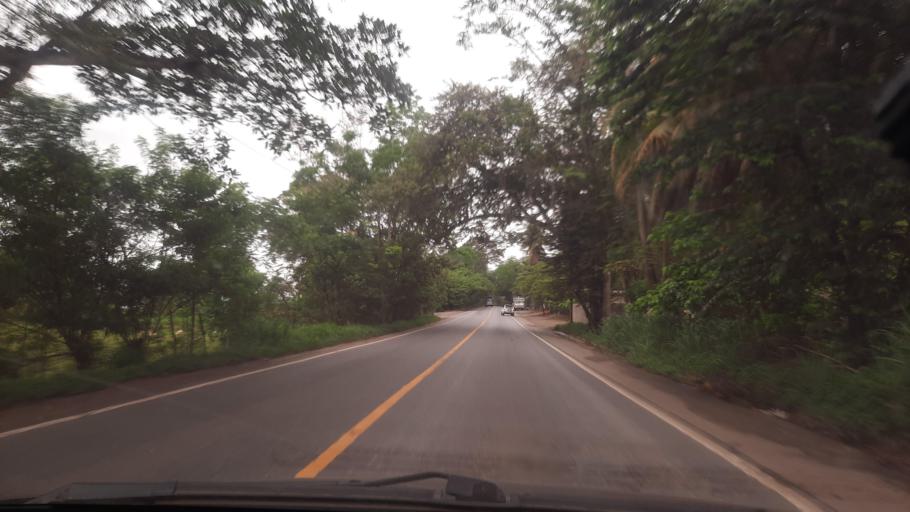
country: GT
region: Izabal
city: Morales
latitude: 15.4322
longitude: -88.9677
